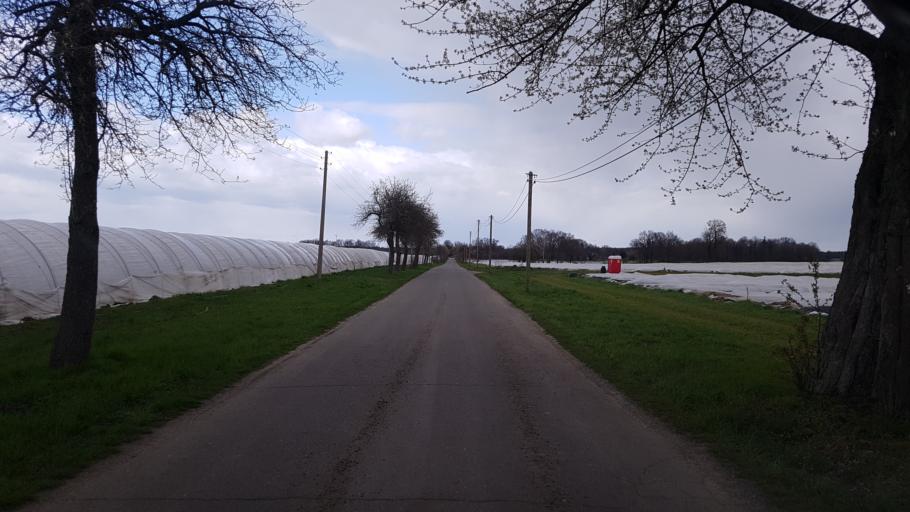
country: DE
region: Brandenburg
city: Calau
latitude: 51.7463
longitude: 14.0028
